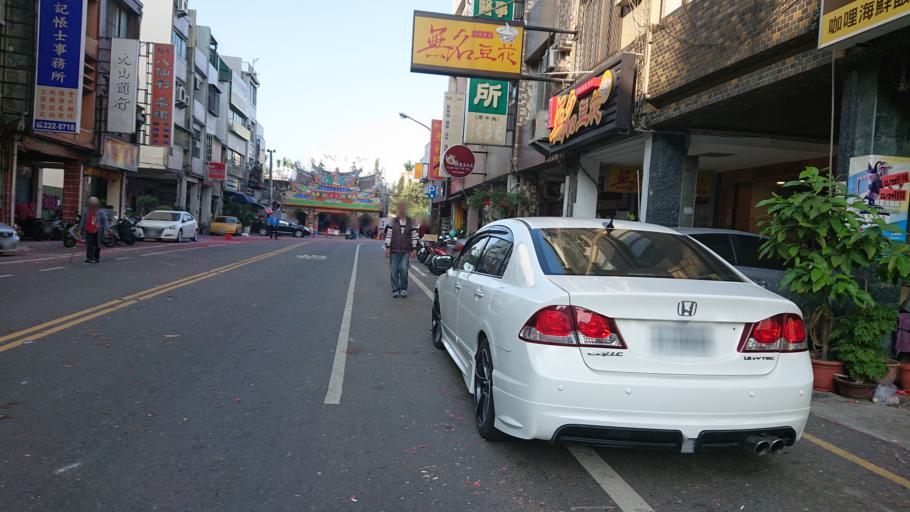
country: TW
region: Taiwan
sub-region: Tainan
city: Tainan
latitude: 22.9956
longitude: 120.2019
